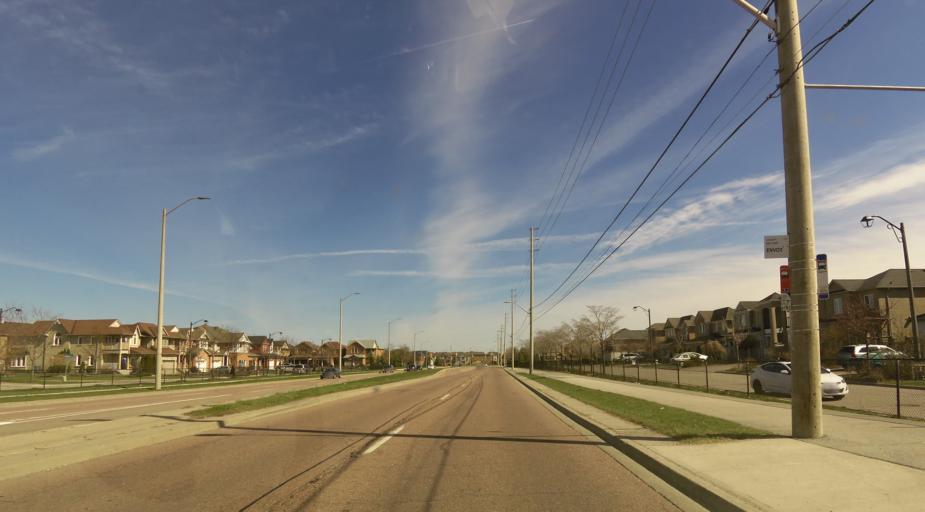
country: CA
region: Ontario
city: Brampton
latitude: 43.6369
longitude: -79.7275
